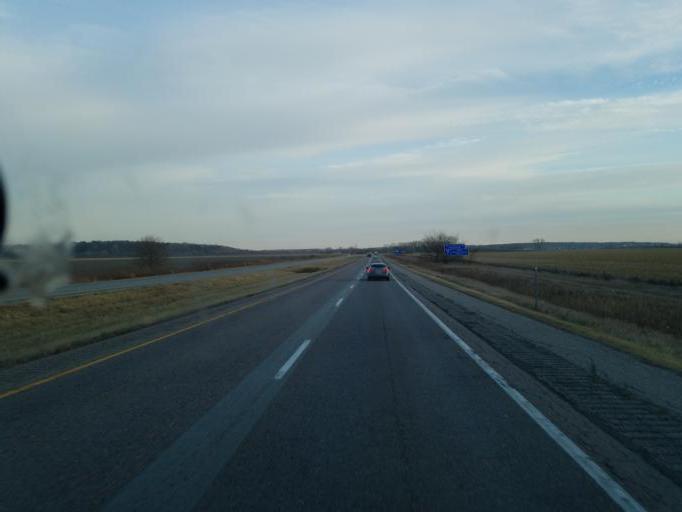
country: US
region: Iowa
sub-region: Harrison County
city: Missouri Valley
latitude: 41.5725
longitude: -95.9262
